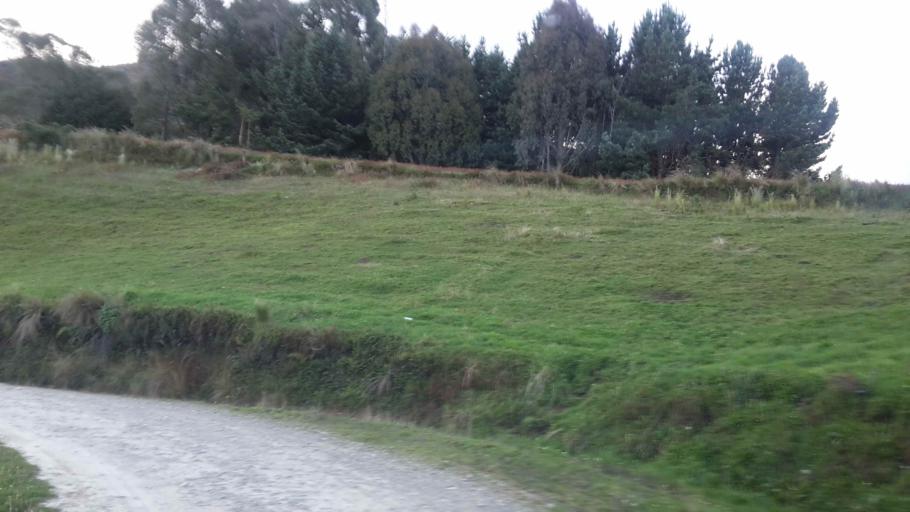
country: BO
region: Cochabamba
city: Colomi
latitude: -17.2643
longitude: -65.9054
